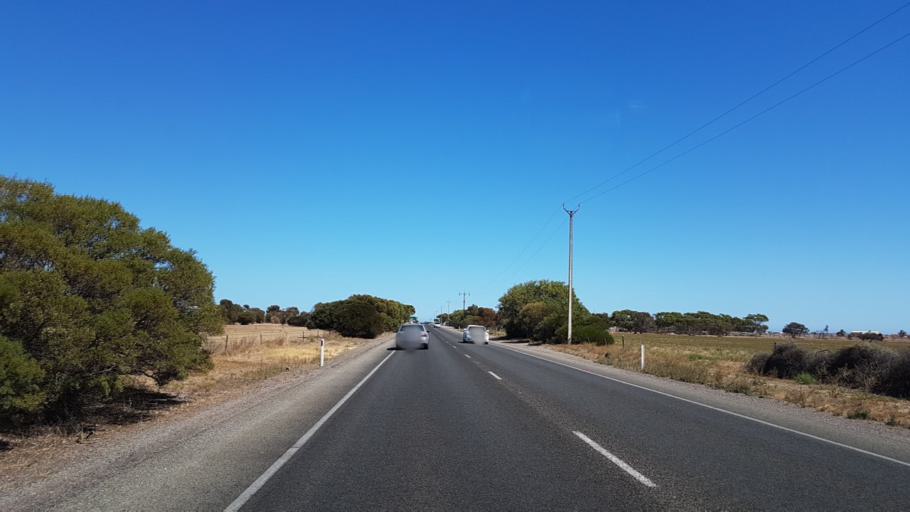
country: AU
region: South Australia
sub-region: Copper Coast
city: Wallaroo
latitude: -33.9432
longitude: 137.6584
